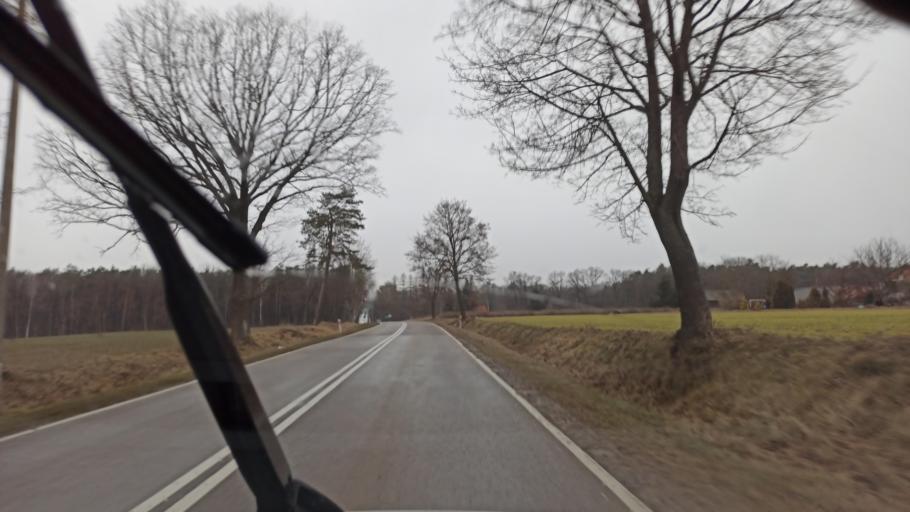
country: PL
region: Lublin Voivodeship
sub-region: Powiat lubelski
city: Strzyzowice
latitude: 51.0383
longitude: 22.4772
